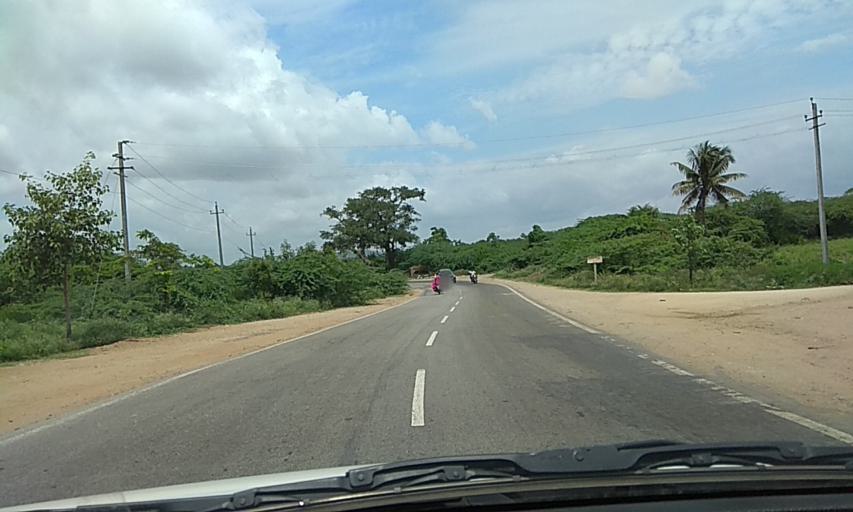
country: IN
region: Karnataka
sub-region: Chamrajnagar
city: Gundlupet
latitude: 11.8108
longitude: 76.7063
